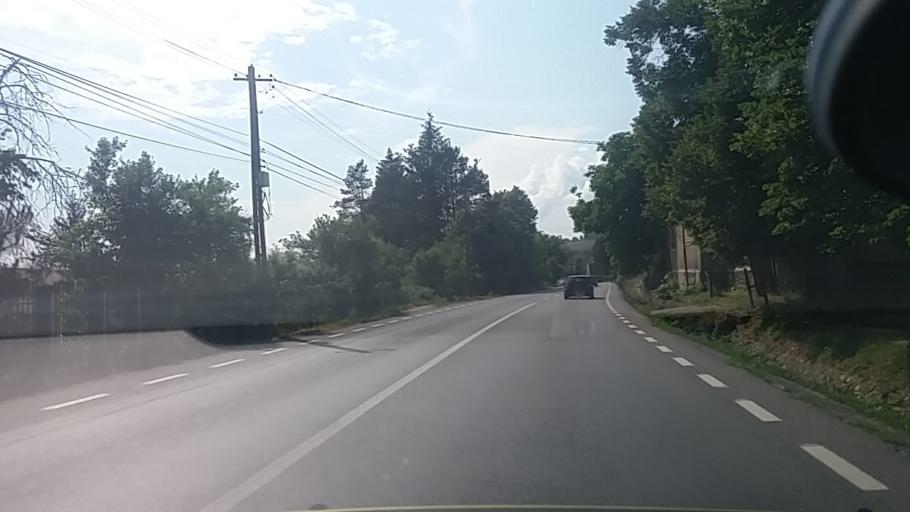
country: RO
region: Arad
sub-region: Comuna Barzava
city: Barzava
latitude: 46.1047
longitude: 21.9996
